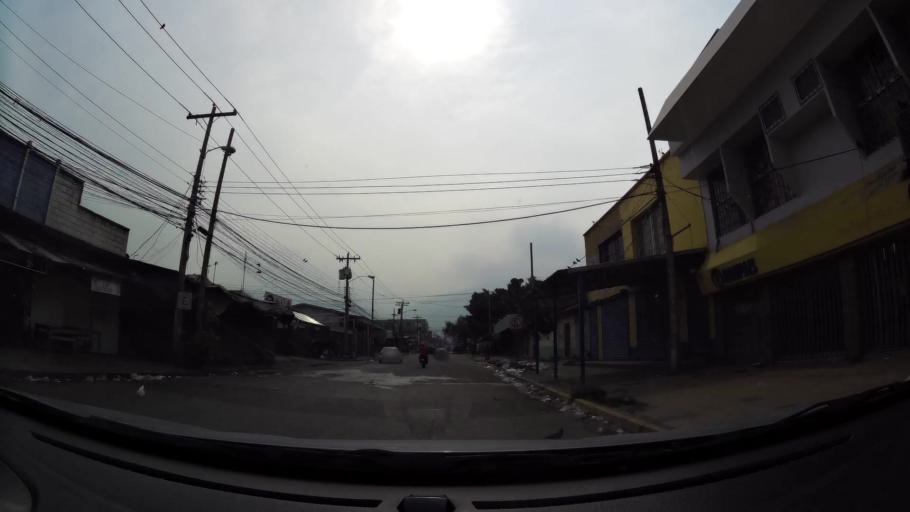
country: HN
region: Cortes
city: San Pedro Sula
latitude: 15.4994
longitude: -88.0161
